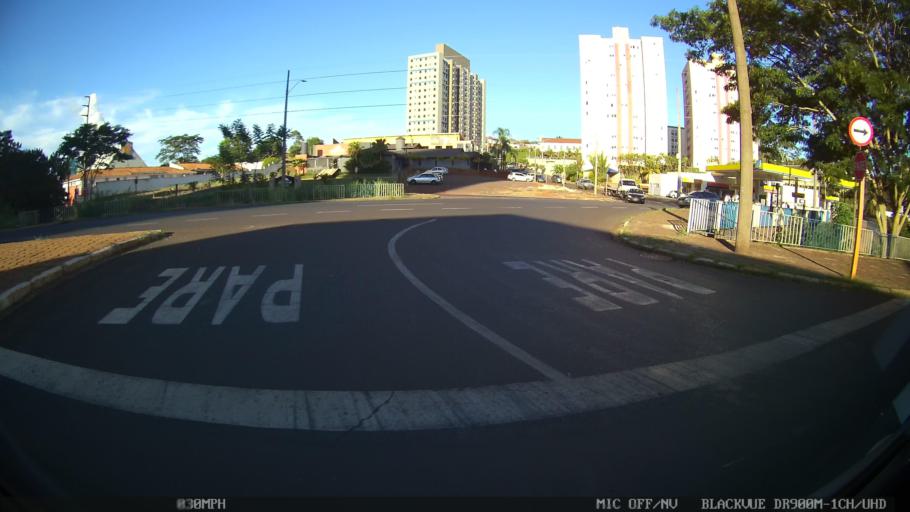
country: BR
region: Sao Paulo
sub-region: Araraquara
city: Araraquara
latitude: -21.8062
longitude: -48.1725
